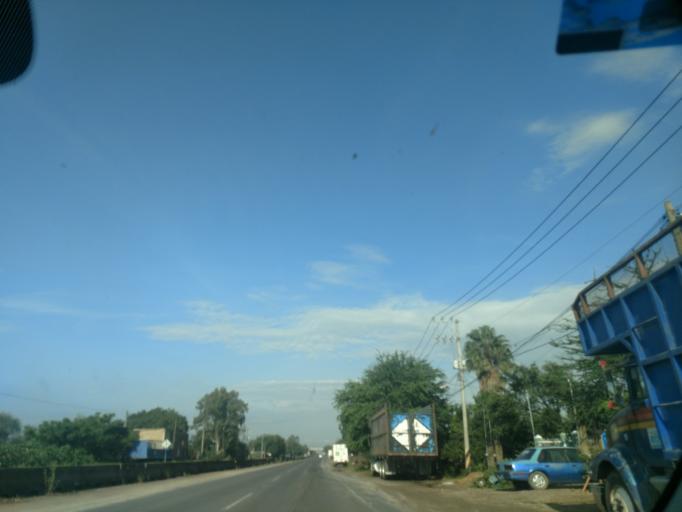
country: MX
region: Jalisco
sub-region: Ameca
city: Los Pocitos
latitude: 20.5376
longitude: -103.9308
